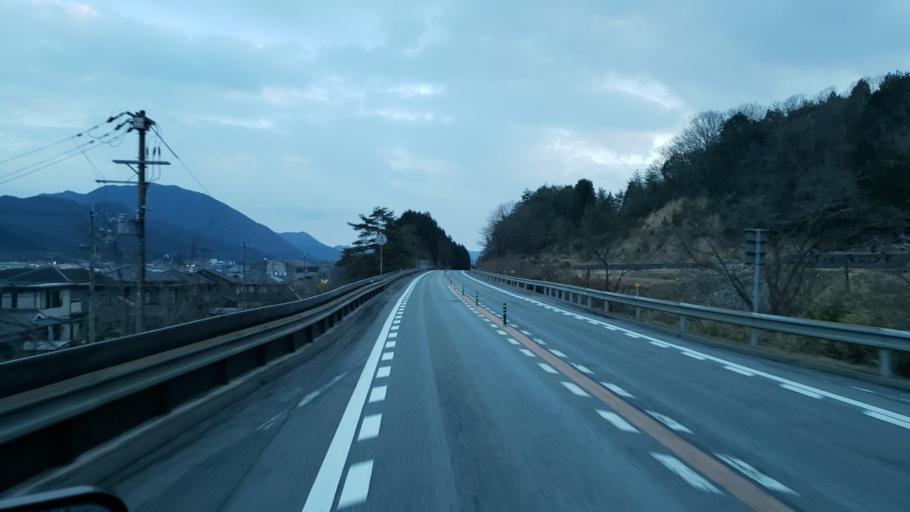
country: JP
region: Hyogo
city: Nishiwaki
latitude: 35.0731
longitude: 134.7703
